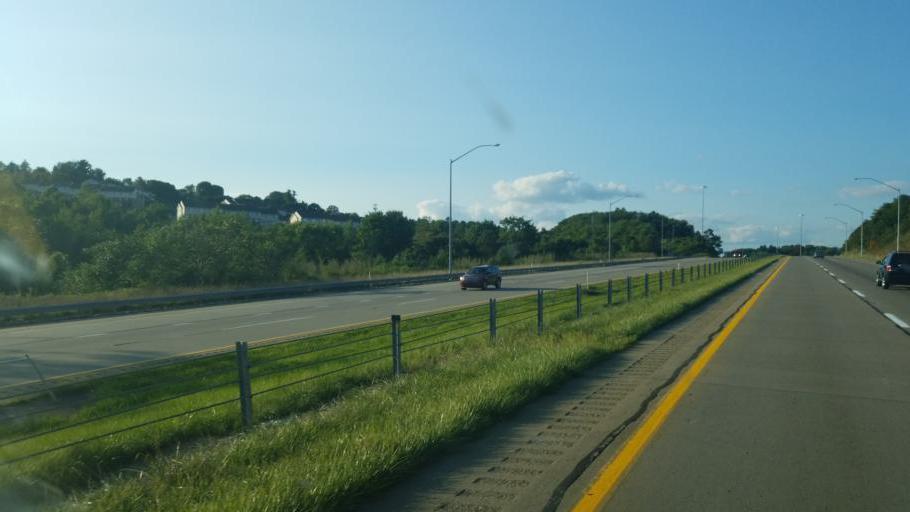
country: US
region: Pennsylvania
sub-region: Allegheny County
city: Ingram
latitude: 40.4434
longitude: -80.1112
